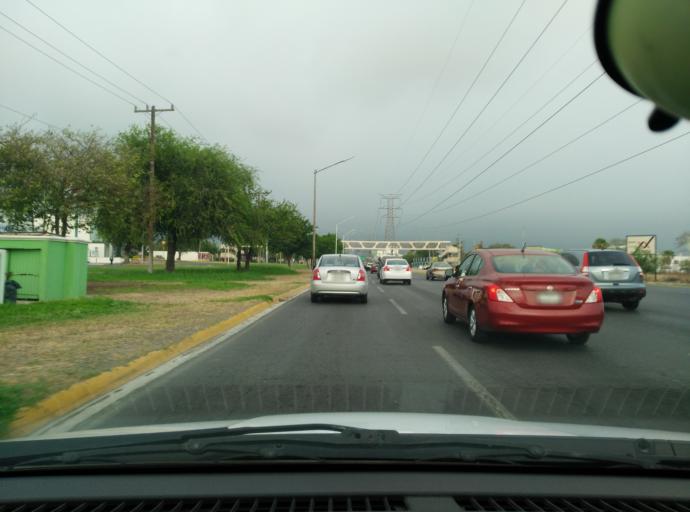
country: MX
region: Nuevo Leon
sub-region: San Nicolas de los Garza
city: San Nicolas de los Garza
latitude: 25.7689
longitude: -100.2820
